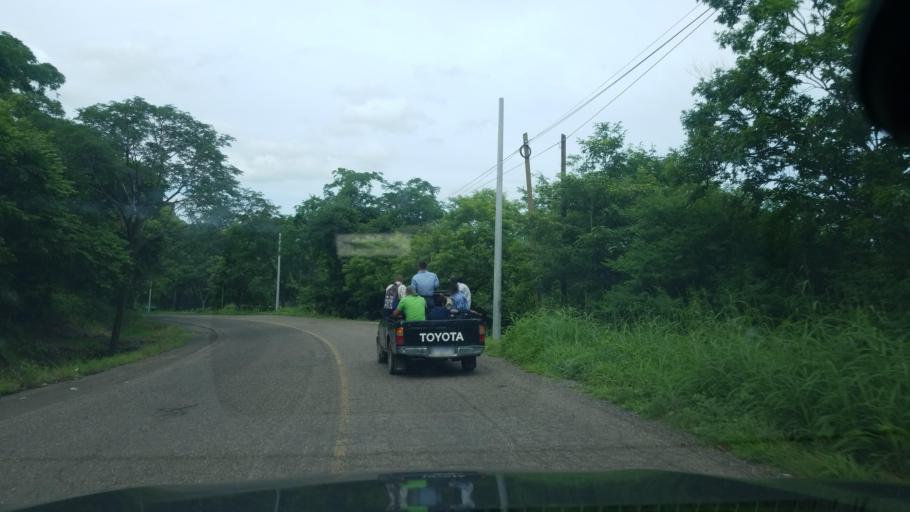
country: HN
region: Choluteca
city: Corpus
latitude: 13.3723
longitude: -87.0519
